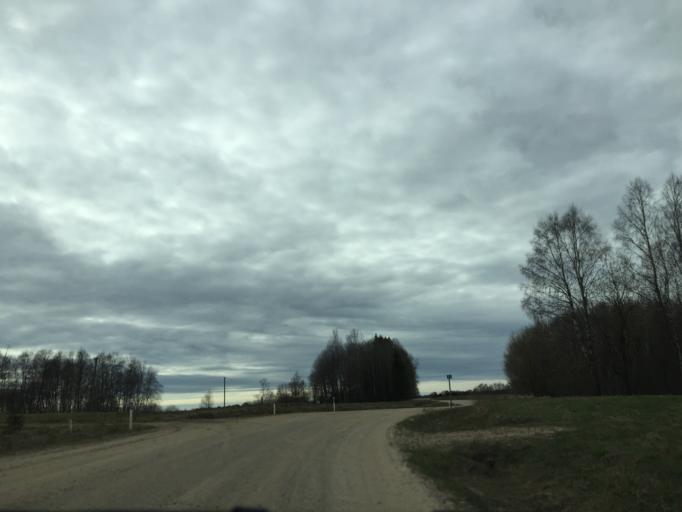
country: LT
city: Silale
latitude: 55.6188
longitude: 22.2041
